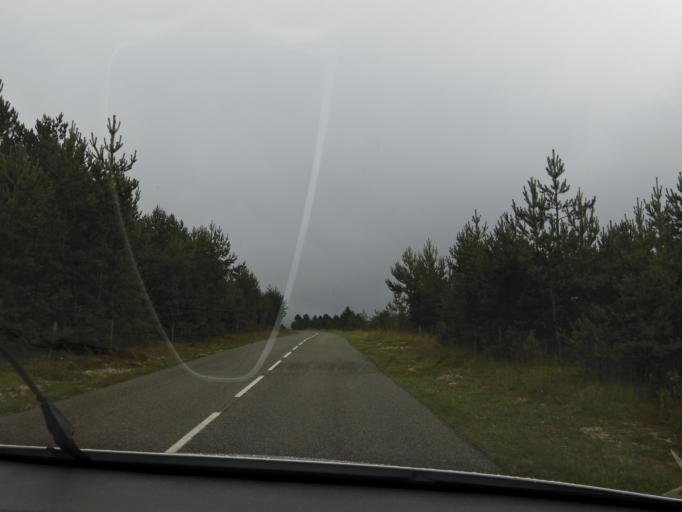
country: FR
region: Languedoc-Roussillon
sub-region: Departement de la Lozere
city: Mende
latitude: 44.4236
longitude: 3.5029
